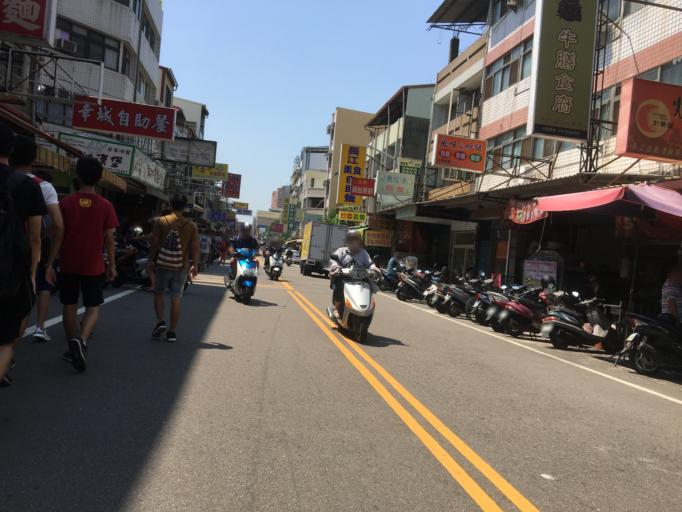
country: TW
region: Taiwan
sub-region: Changhua
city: Chang-hua
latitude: 24.0836
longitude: 120.5580
